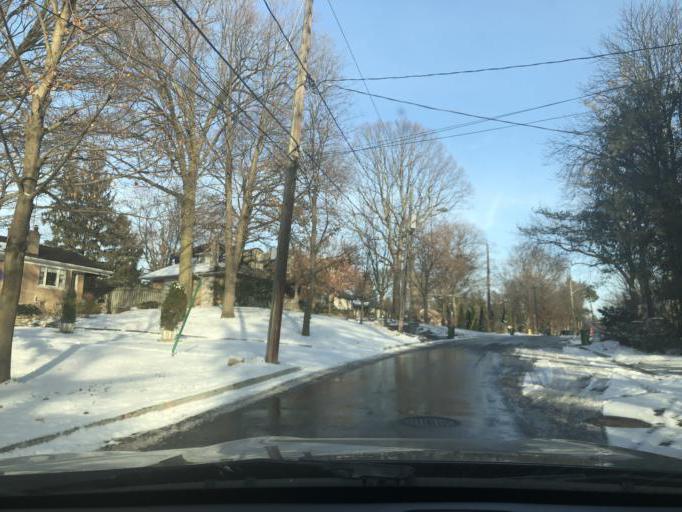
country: CA
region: Ontario
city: Toronto
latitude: 43.6955
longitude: -79.4826
